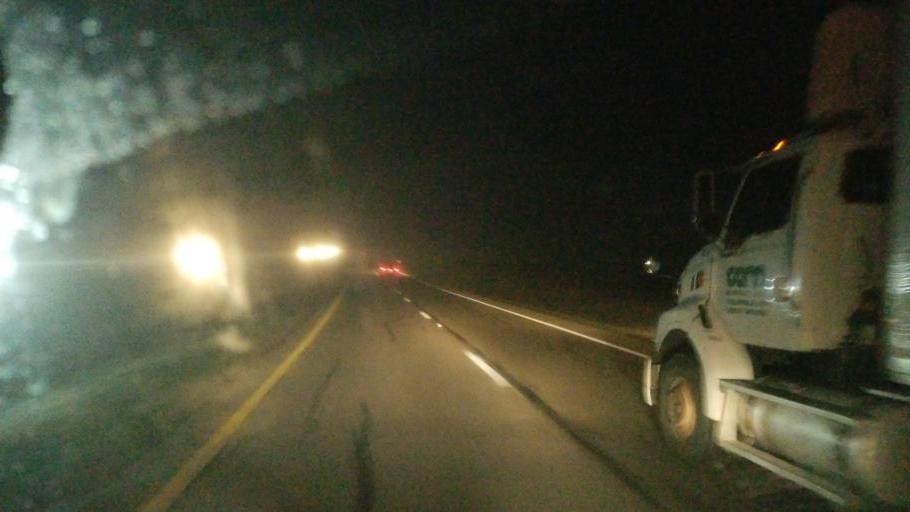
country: US
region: Ohio
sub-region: Pickaway County
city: Logan Elm Village
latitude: 39.5374
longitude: -82.9671
